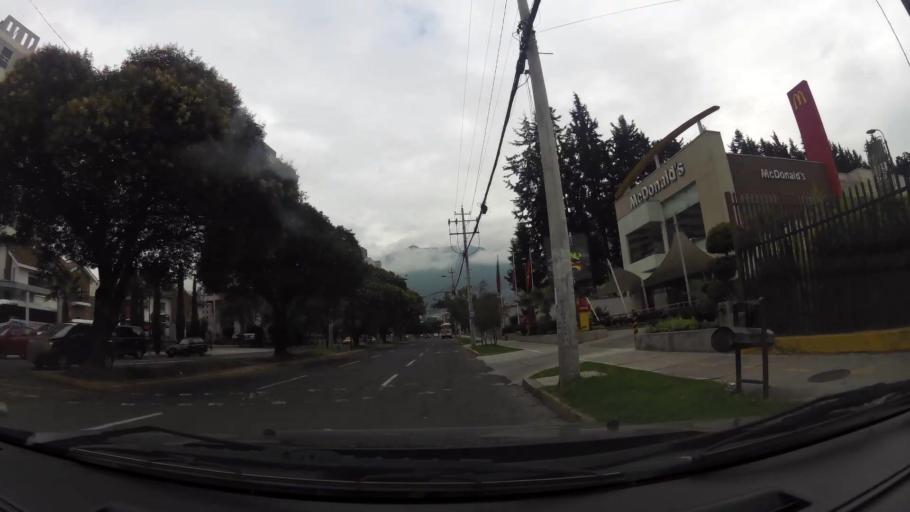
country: EC
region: Pichincha
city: Quito
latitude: -0.1978
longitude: -78.4875
